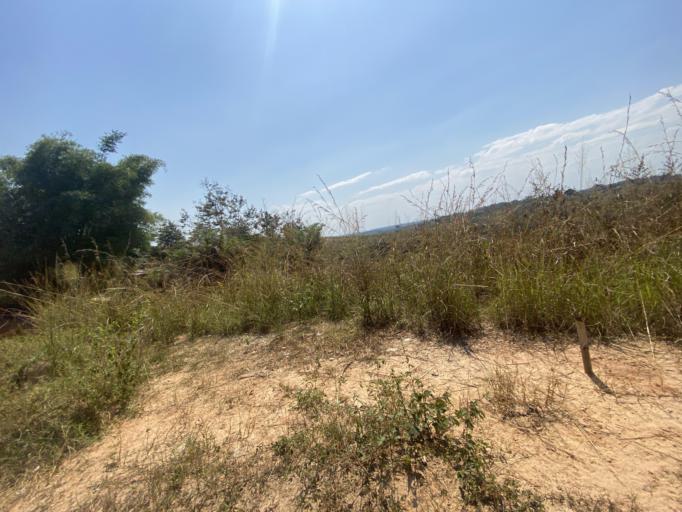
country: CD
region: Kasai-Oriental
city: Kabinda
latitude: -6.1468
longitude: 24.1952
